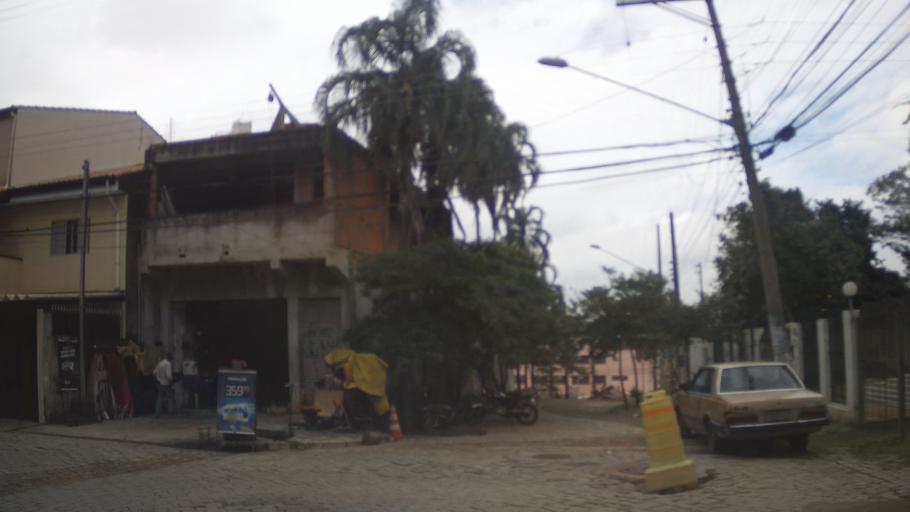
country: BR
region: Sao Paulo
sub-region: Guarulhos
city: Guarulhos
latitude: -23.4679
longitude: -46.5495
